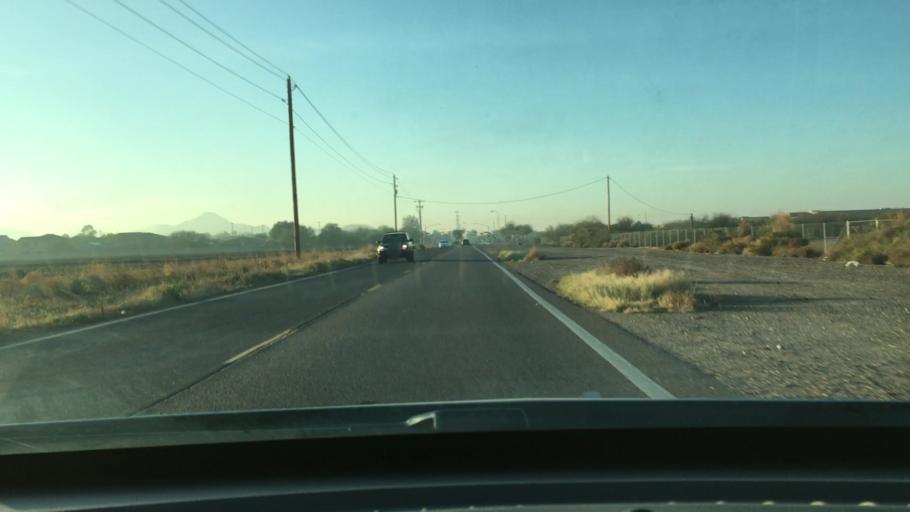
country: US
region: Arizona
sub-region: Maricopa County
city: Chandler
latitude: 33.2254
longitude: -111.7555
